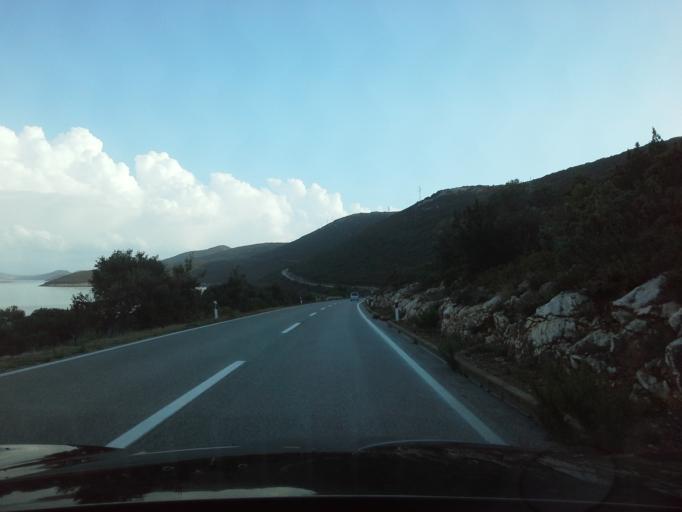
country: HR
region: Primorsko-Goranska
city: Mali Losinj
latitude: 44.6327
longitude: 14.3923
